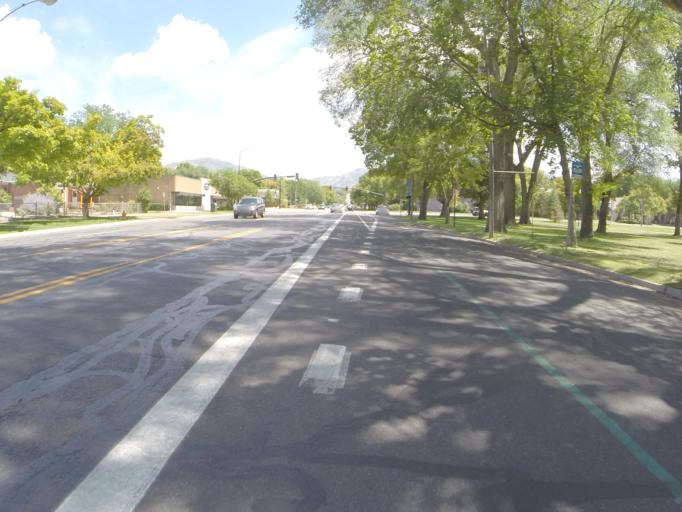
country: US
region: Utah
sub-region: Salt Lake County
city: Salt Lake City
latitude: 40.7497
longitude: -111.8723
